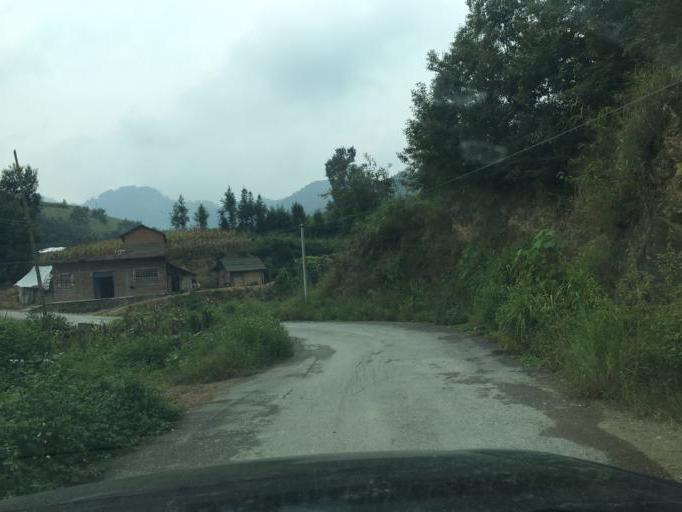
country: CN
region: Guangxi Zhuangzu Zizhiqu
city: Tongle
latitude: 25.1118
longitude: 106.2707
